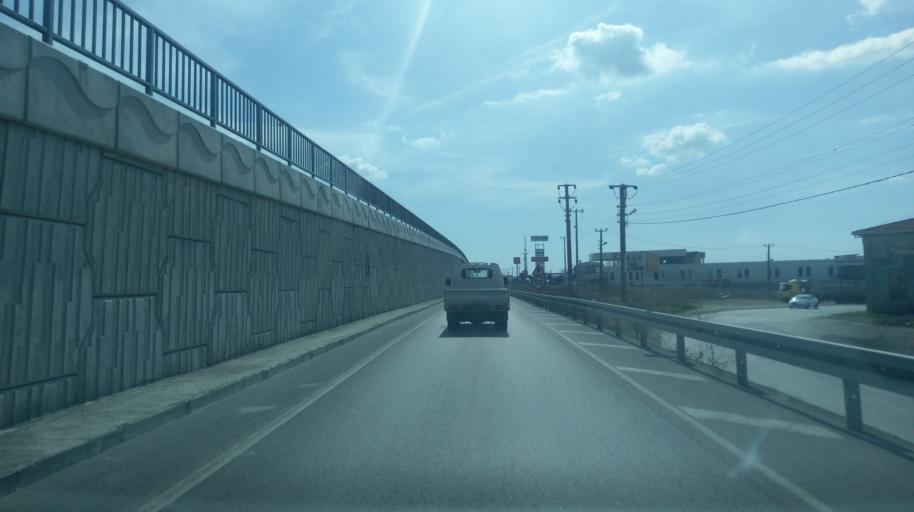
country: TR
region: Edirne
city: Kesan
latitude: 40.8602
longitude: 26.6217
